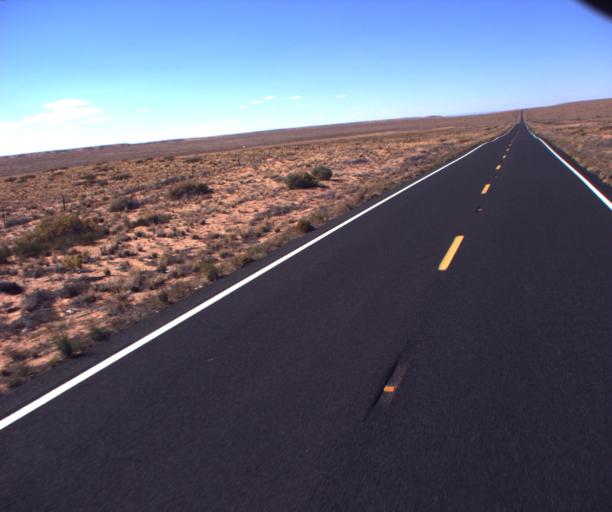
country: US
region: Arizona
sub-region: Coconino County
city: Tuba City
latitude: 36.0262
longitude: -111.1491
